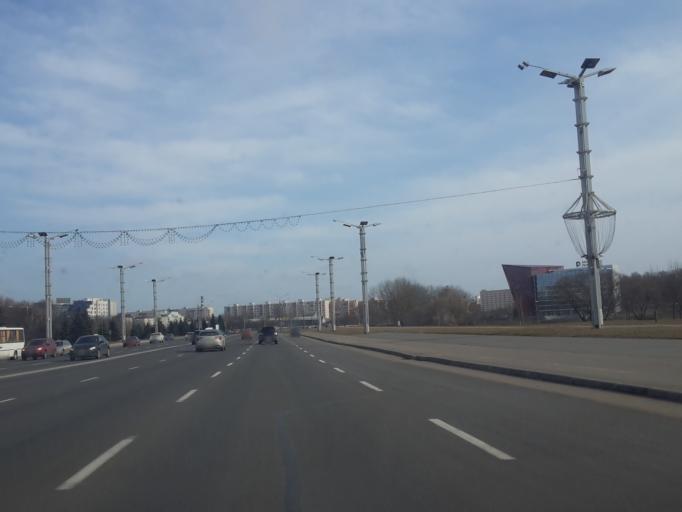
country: BY
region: Minsk
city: Minsk
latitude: 53.9151
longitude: 27.5410
